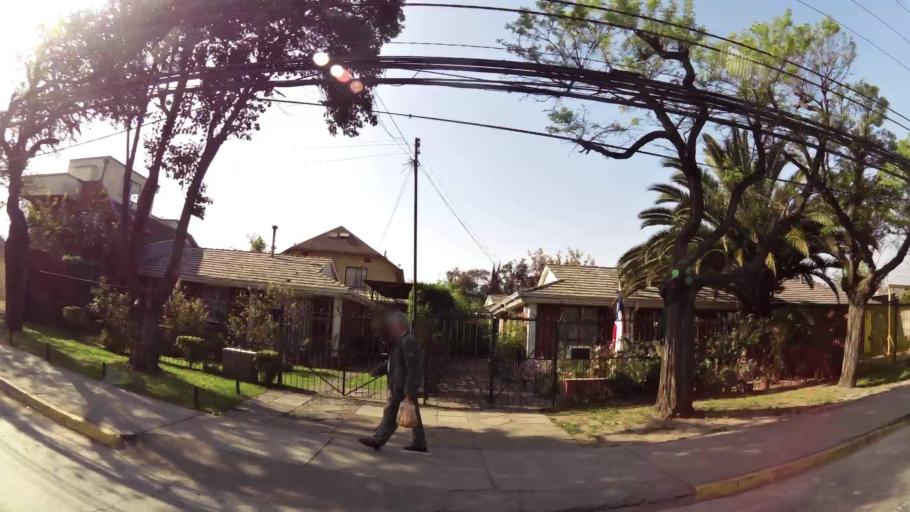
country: CL
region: Santiago Metropolitan
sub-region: Provincia de Santiago
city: Villa Presidente Frei, Nunoa, Santiago, Chile
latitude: -33.4617
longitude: -70.5765
